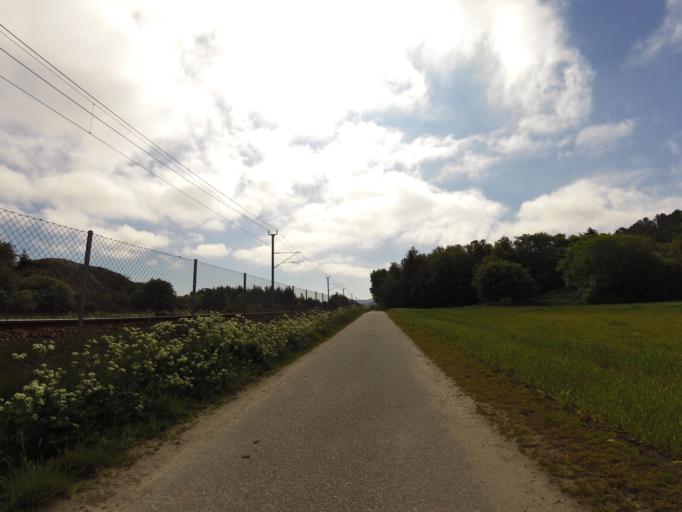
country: NO
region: Rogaland
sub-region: Ha
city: Vigrestad
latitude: 58.5244
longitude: 5.7915
